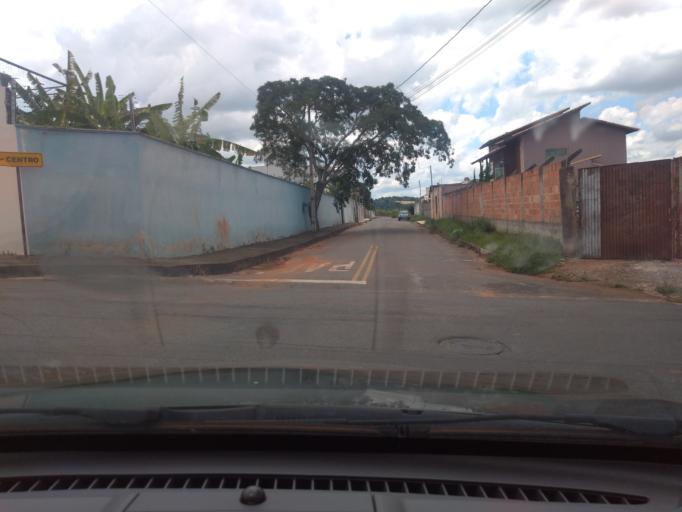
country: BR
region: Minas Gerais
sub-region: Tres Coracoes
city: Tres Coracoes
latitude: -21.6687
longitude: -45.2722
